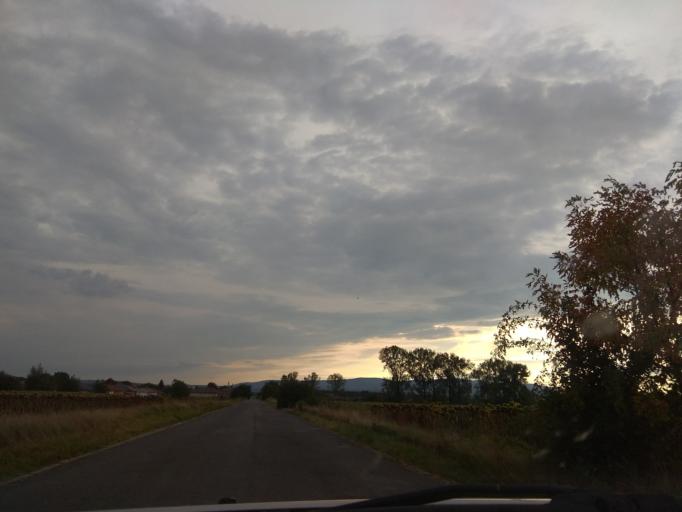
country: HU
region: Borsod-Abauj-Zemplen
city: Felsozsolca
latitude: 48.0769
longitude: 20.8358
